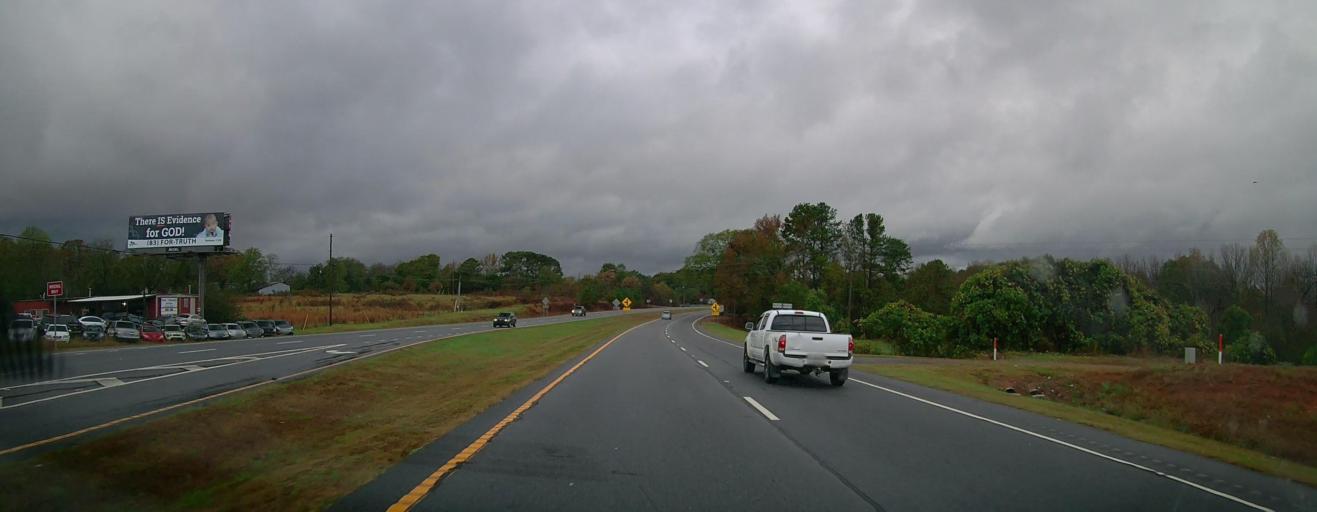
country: US
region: Georgia
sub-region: Jackson County
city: Nicholson
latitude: 34.0980
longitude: -83.4316
